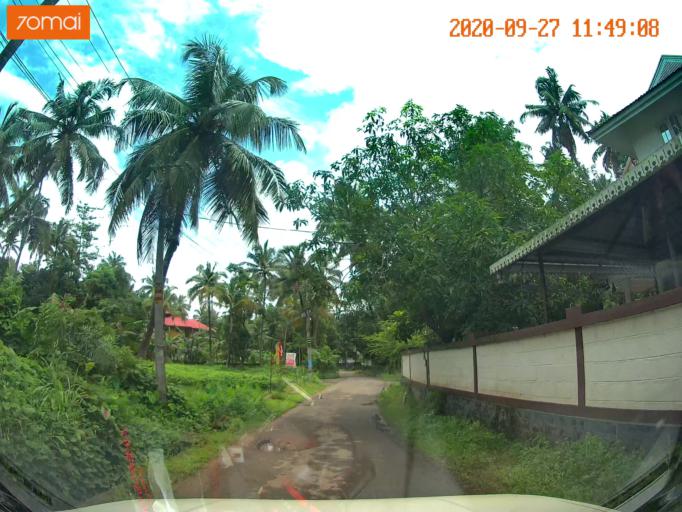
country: IN
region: Kerala
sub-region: Thrissur District
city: Thanniyam
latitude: 10.4715
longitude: 76.1141
